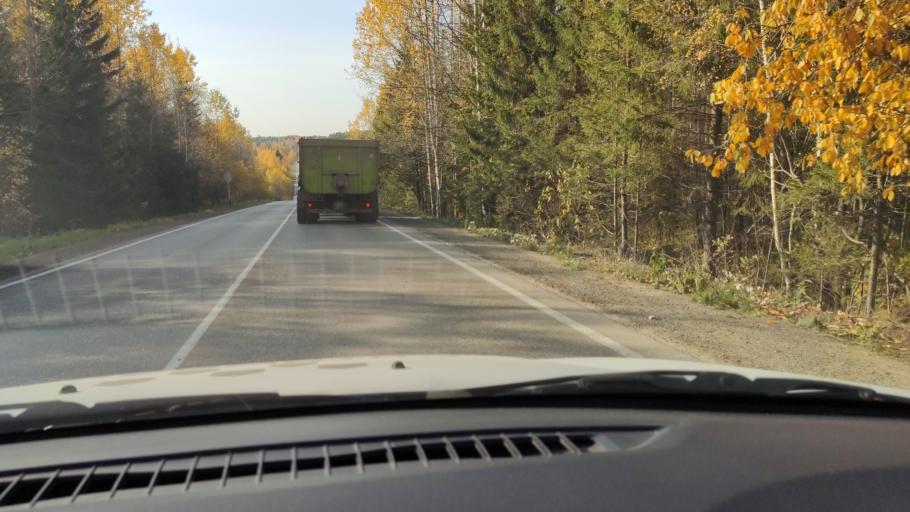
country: RU
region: Perm
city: Novyye Lyady
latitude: 58.0280
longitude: 56.6816
